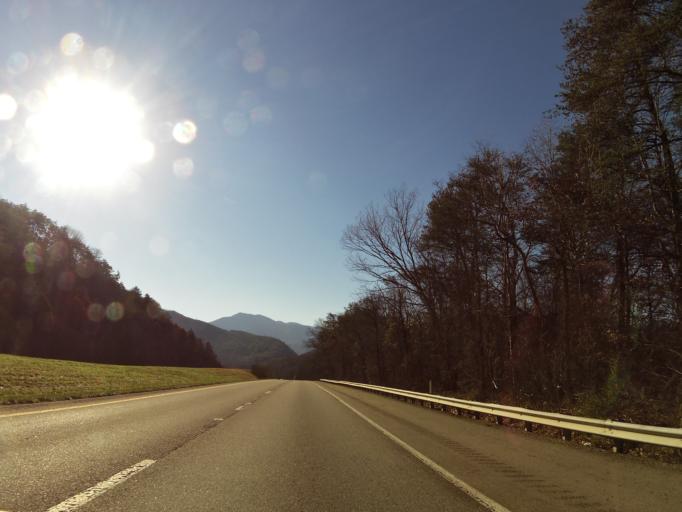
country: US
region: Tennessee
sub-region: Cocke County
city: Newport
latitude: 35.8506
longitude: -83.1836
